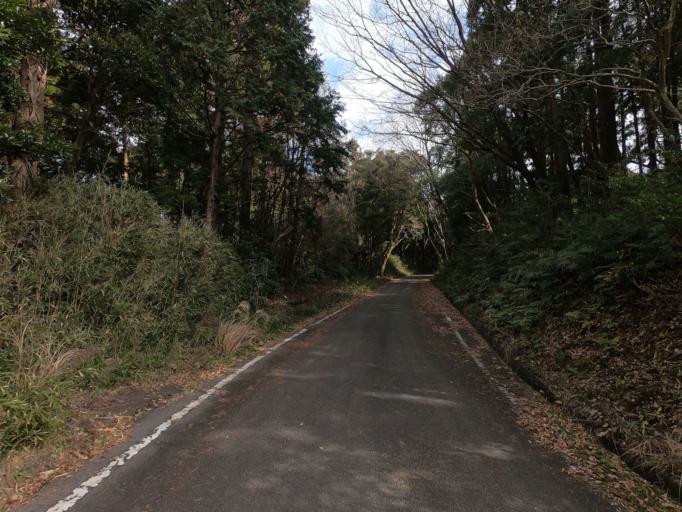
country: JP
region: Ibaraki
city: Inashiki
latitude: 36.0586
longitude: 140.4422
